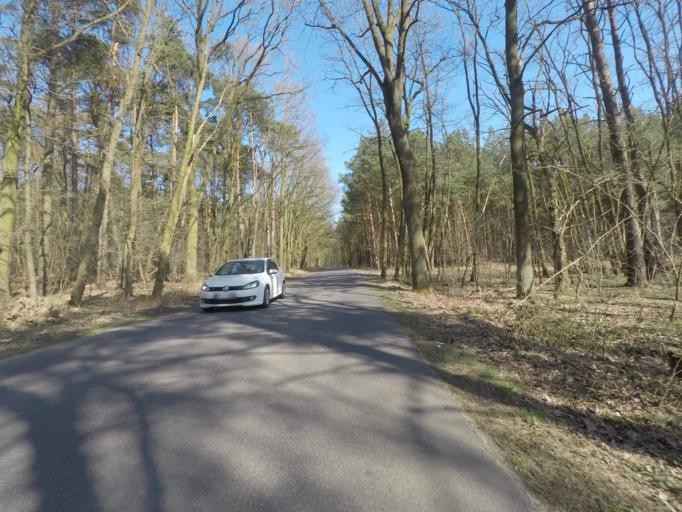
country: DE
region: Brandenburg
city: Melchow
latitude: 52.8632
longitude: 13.7031
